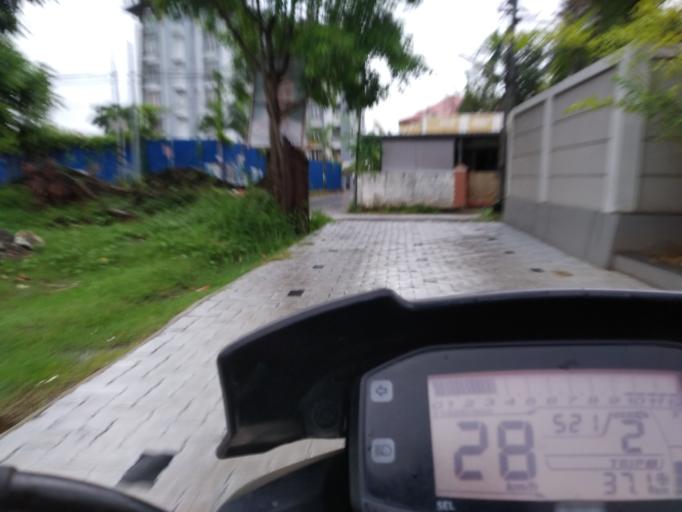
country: IN
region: Kerala
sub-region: Ernakulam
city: Cochin
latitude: 9.9773
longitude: 76.3074
